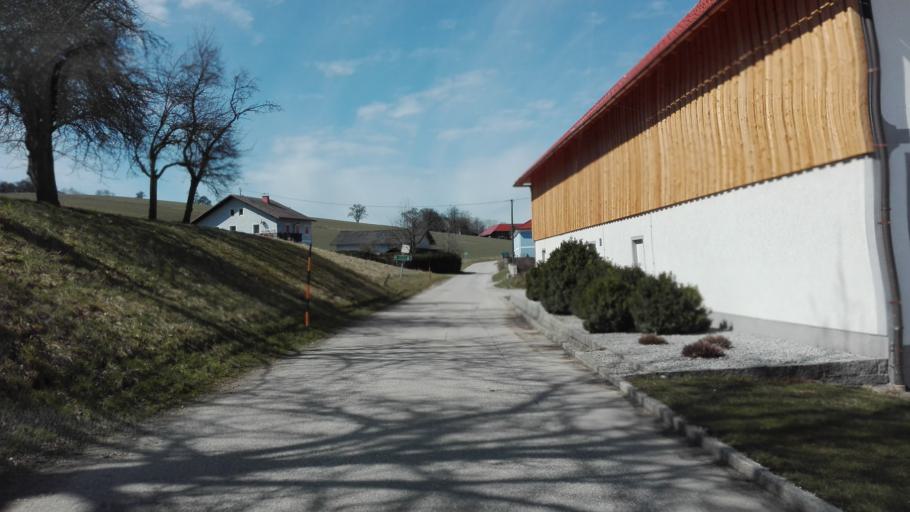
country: AT
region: Upper Austria
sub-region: Politischer Bezirk Grieskirchen
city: Bad Schallerbach
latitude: 48.2337
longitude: 13.8883
